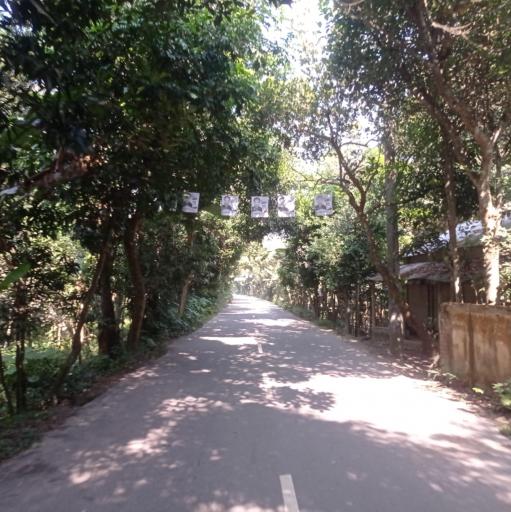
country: BD
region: Dhaka
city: Narsingdi
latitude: 24.0753
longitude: 90.6935
